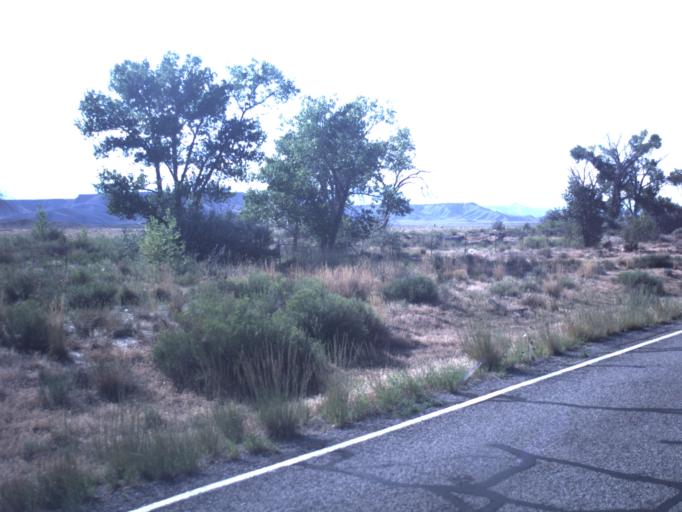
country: US
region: Utah
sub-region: Emery County
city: Huntington
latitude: 39.4199
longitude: -110.8582
